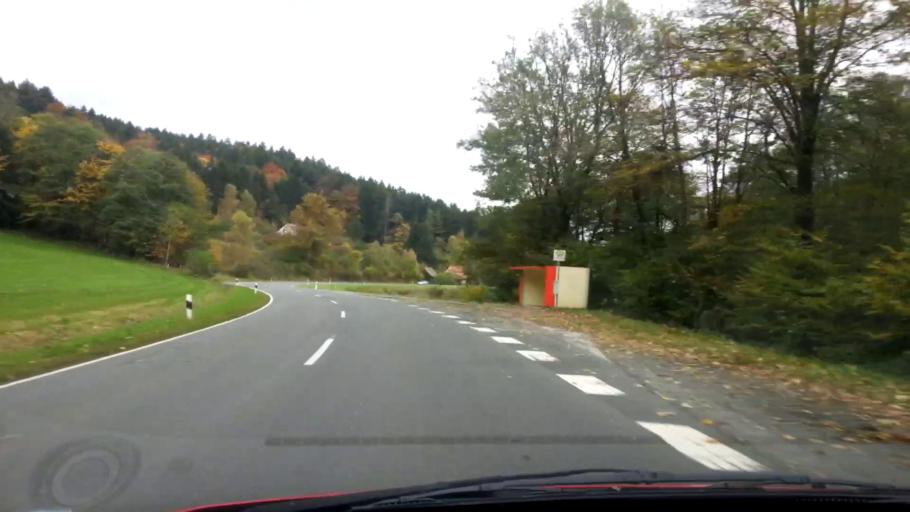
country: DE
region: Bavaria
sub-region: Upper Franconia
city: Kirchenpingarten
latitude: 49.9470
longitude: 11.7552
